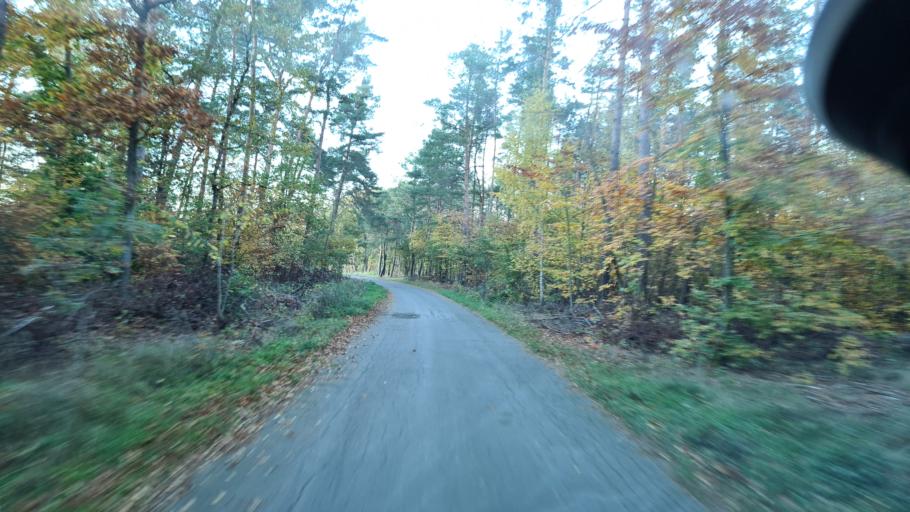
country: DE
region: Saxony
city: Belgern
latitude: 51.4385
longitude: 13.1144
